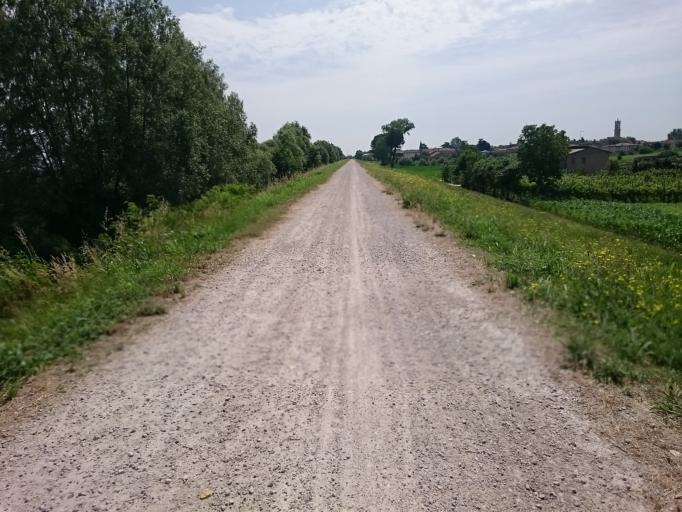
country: IT
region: Veneto
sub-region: Provincia di Padova
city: Correzzola
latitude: 45.2396
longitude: 12.0598
